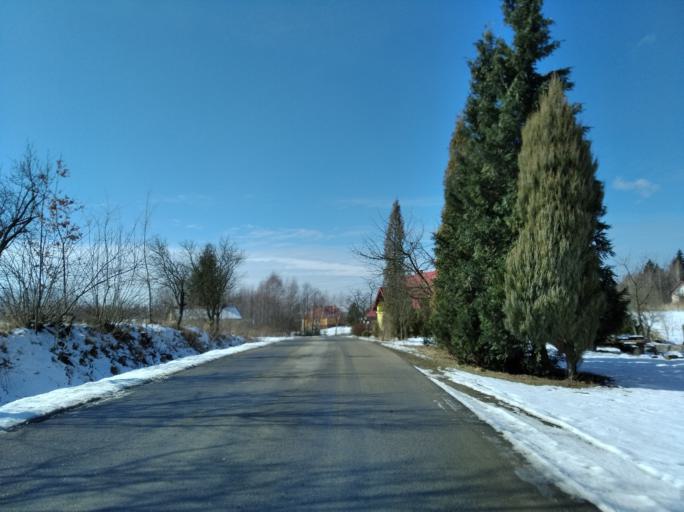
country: PL
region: Subcarpathian Voivodeship
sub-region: Powiat brzozowski
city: Jablonica Polska
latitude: 49.7184
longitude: 21.8976
